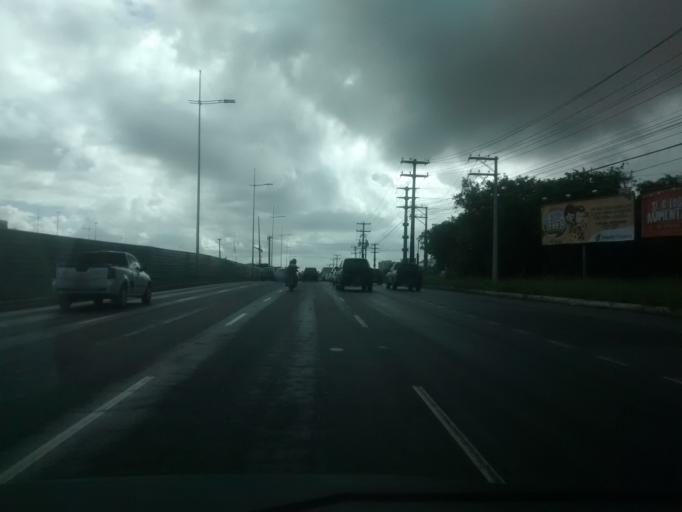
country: BR
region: Bahia
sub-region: Salvador
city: Salvador
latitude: -12.9501
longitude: -38.4243
